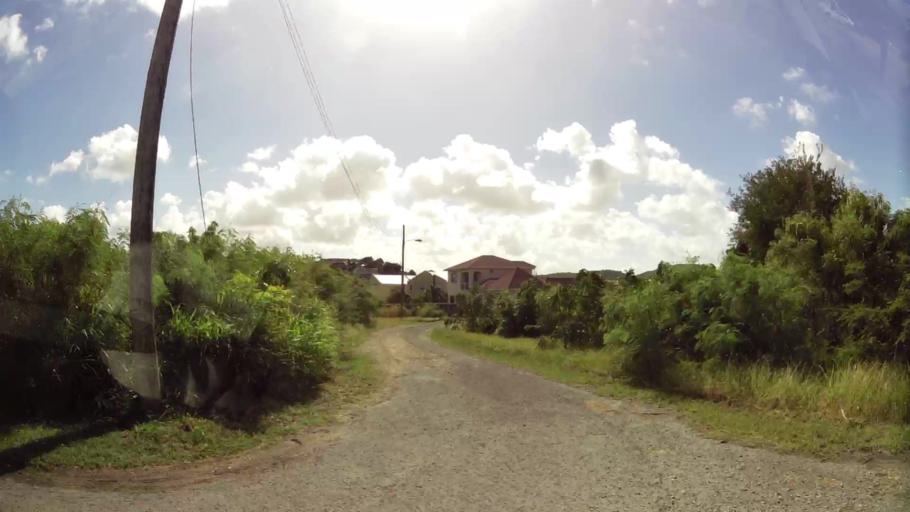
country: AG
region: Saint George
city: Piggotts
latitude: 17.1662
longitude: -61.8062
